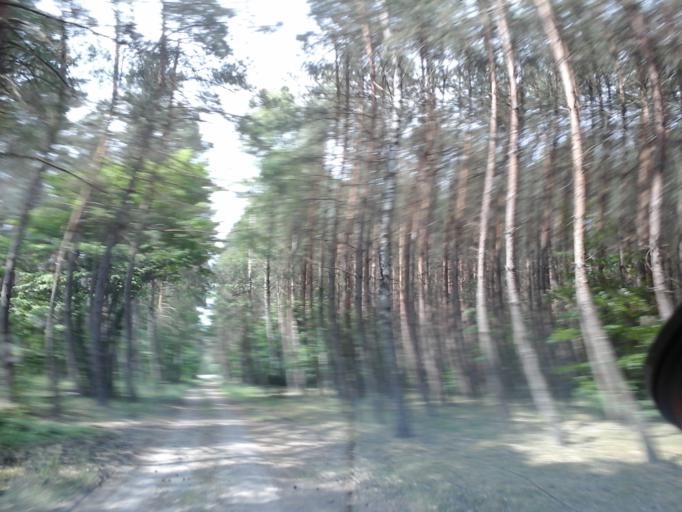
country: PL
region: West Pomeranian Voivodeship
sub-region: Powiat choszczenski
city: Drawno
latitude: 53.1238
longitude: 15.8524
